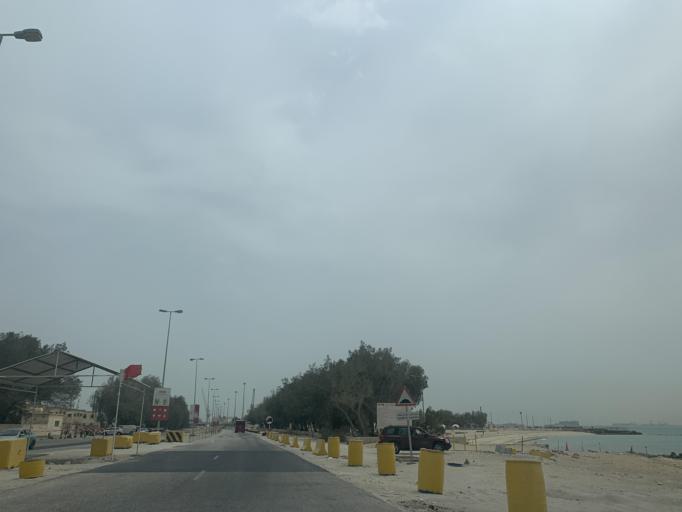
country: BH
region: Muharraq
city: Al Hadd
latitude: 26.1985
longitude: 50.6622
